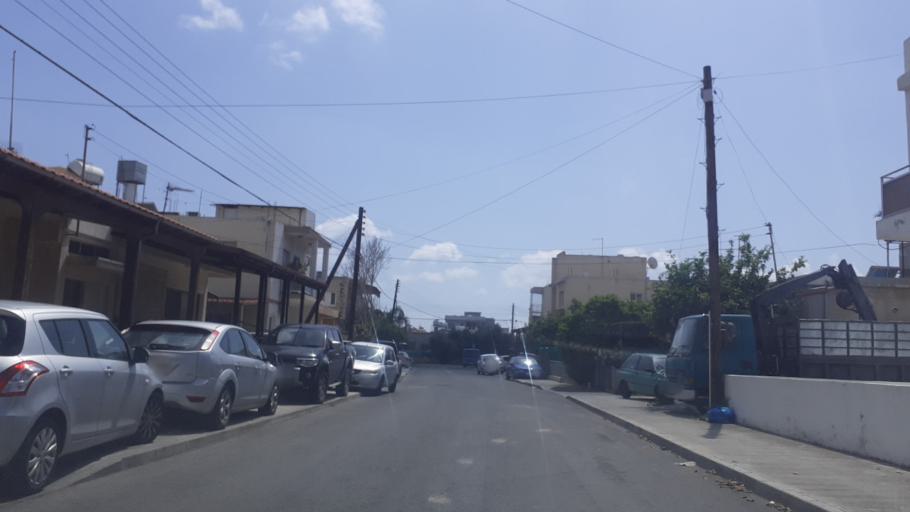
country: CY
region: Limassol
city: Limassol
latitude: 34.6722
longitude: 33.0103
